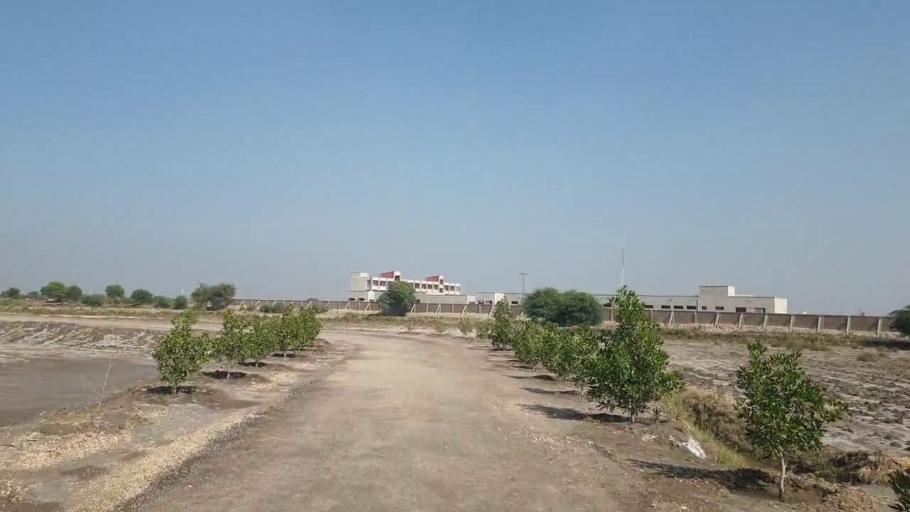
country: PK
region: Sindh
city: Sehwan
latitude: 26.4267
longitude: 67.8333
